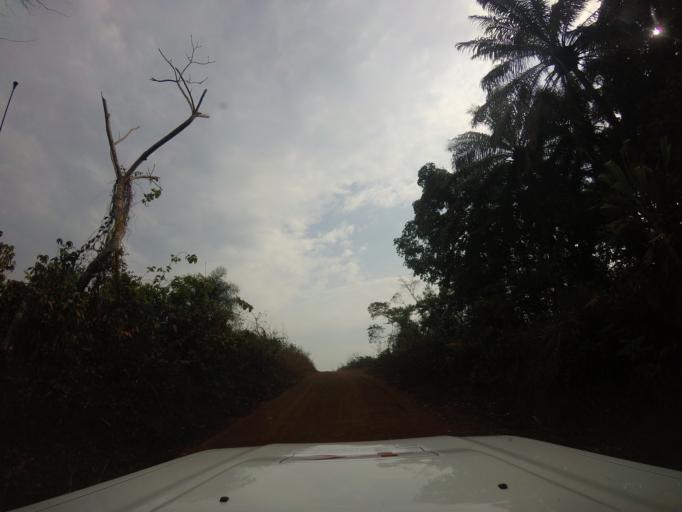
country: LR
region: Grand Cape Mount
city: Robertsport
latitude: 7.0068
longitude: -11.2917
